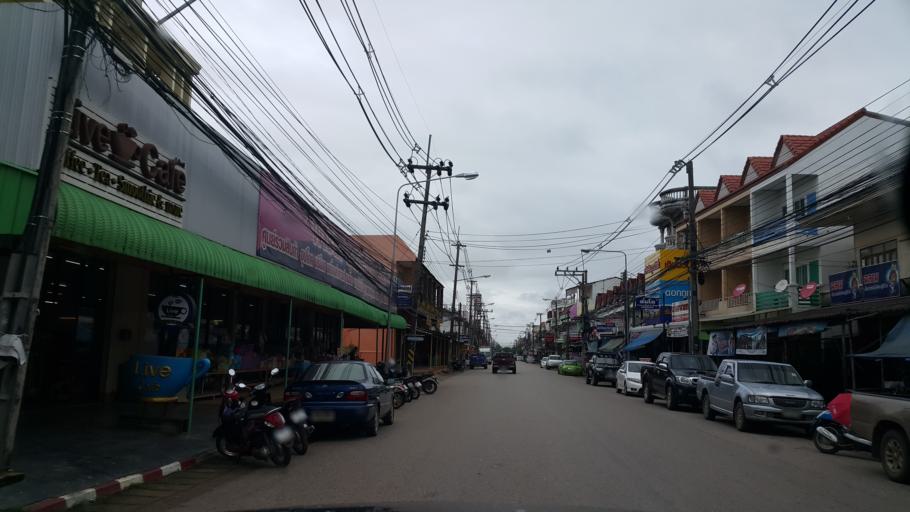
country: TH
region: Phayao
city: Chiang Kham
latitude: 19.5265
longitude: 100.3026
